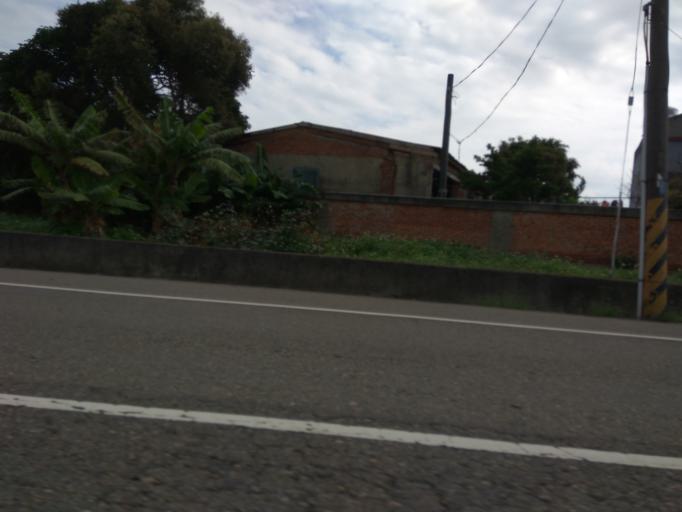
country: TW
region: Taiwan
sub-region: Hsinchu
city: Zhubei
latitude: 24.9637
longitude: 121.0149
